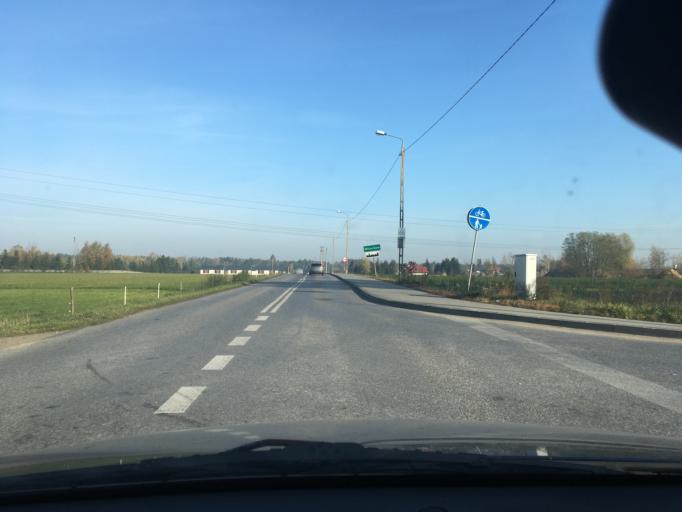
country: PL
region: Masovian Voivodeship
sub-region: Powiat piaseczynski
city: Lesznowola
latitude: 52.0701
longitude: 20.9348
